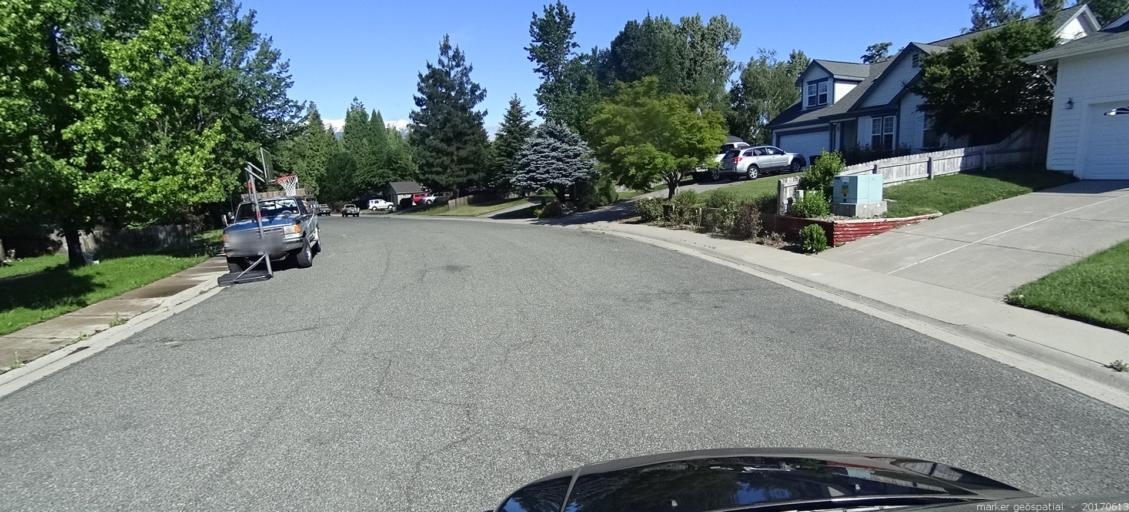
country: US
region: California
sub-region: Siskiyou County
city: Mount Shasta
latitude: 41.3038
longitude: -122.3042
